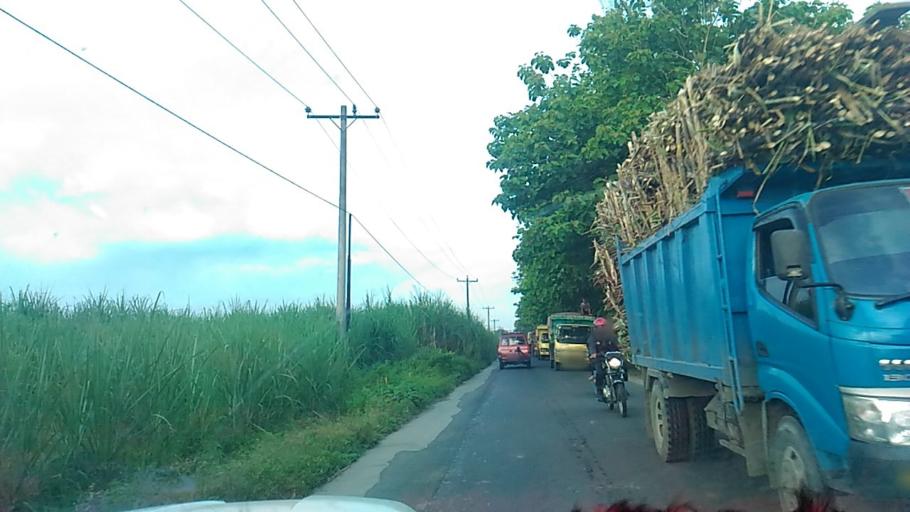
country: ID
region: North Sumatra
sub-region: Kabupaten Langkat
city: Stabat
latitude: 3.7042
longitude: 98.5578
